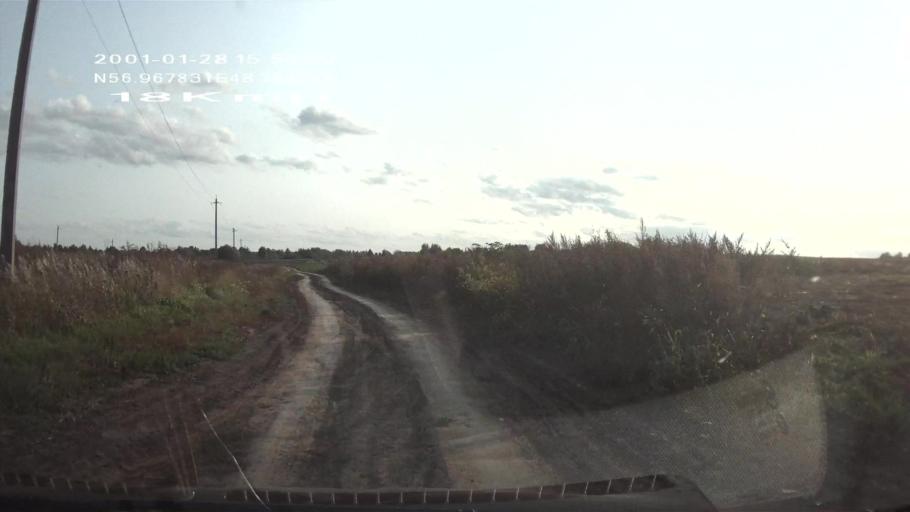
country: RU
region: Mariy-El
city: Kuzhener
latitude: 56.9676
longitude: 48.7839
